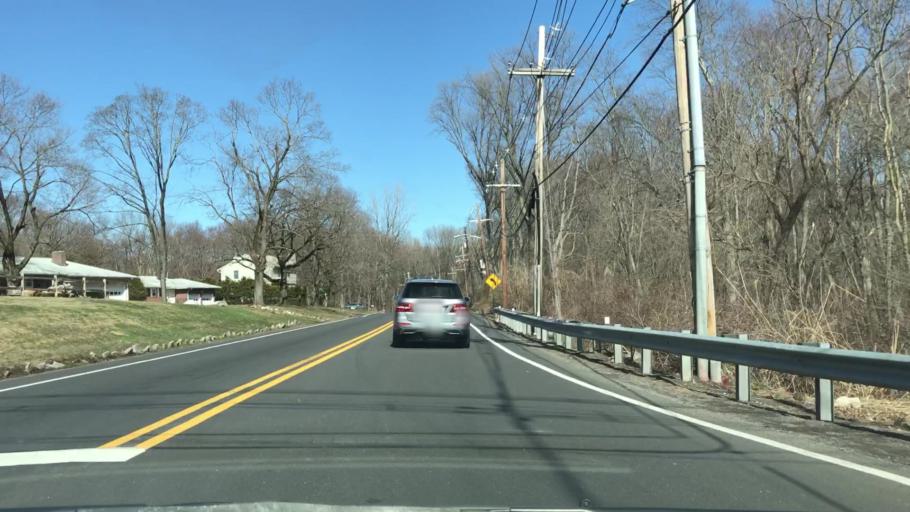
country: US
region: New Jersey
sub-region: Bergen County
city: Norwood
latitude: 40.9859
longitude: -73.9609
